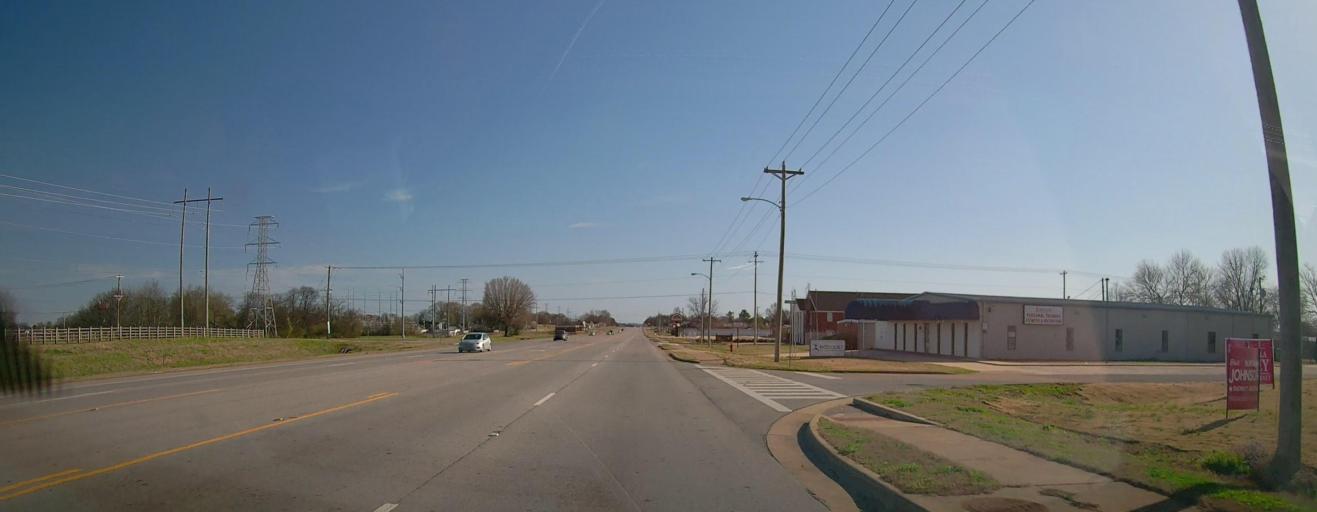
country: US
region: Alabama
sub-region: Colbert County
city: Muscle Shoals
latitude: 34.7415
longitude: -87.6354
